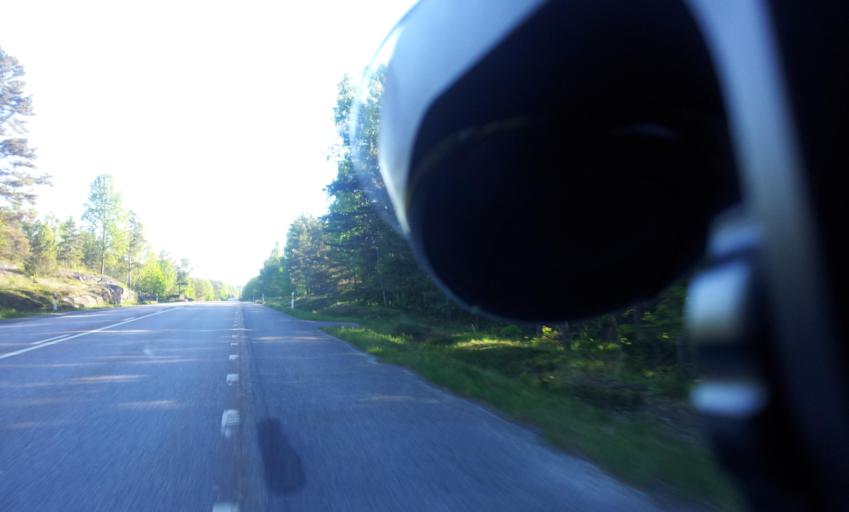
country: SE
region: Kalmar
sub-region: Vasterviks Kommun
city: Ankarsrum
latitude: 57.6956
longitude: 16.4409
